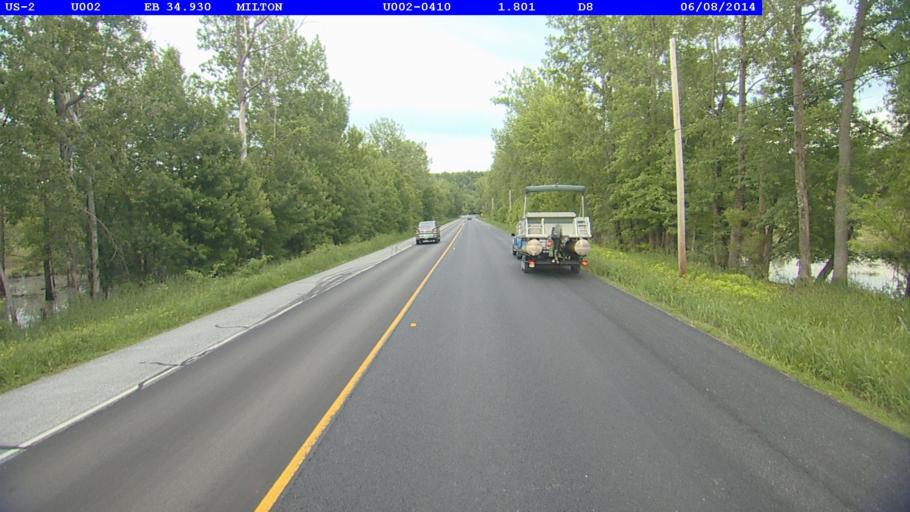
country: US
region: Vermont
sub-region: Chittenden County
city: Colchester
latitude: 44.6240
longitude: -73.2215
